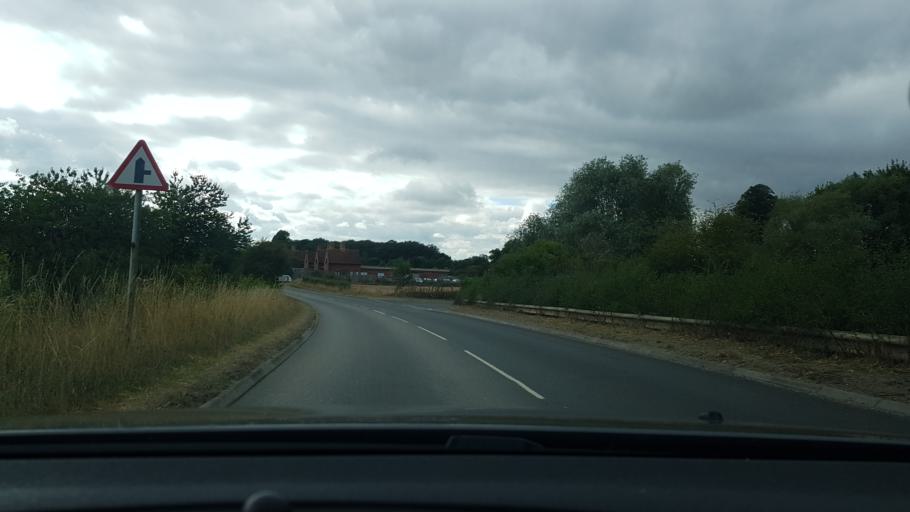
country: GB
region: England
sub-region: West Berkshire
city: Hermitage
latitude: 51.4576
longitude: -1.2934
